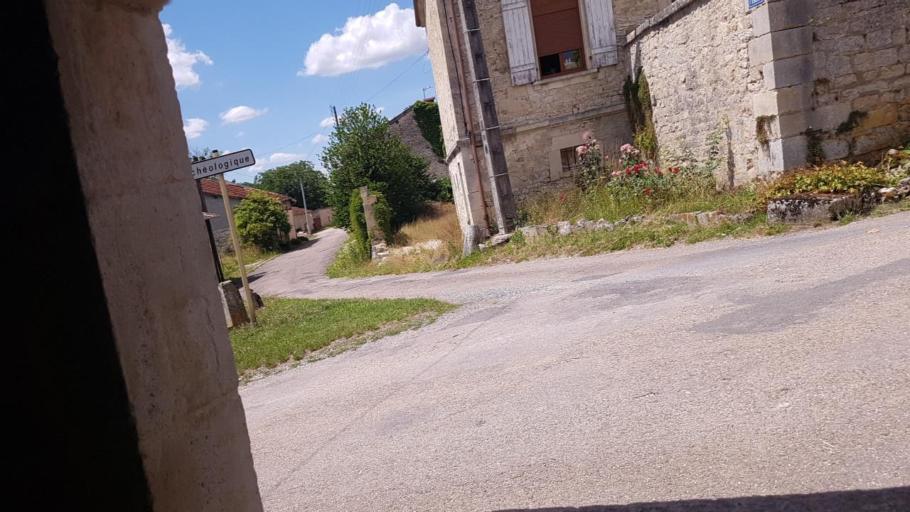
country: FR
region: Lorraine
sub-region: Departement de la Meuse
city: Ligny-en-Barrois
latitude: 48.6473
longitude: 5.4170
